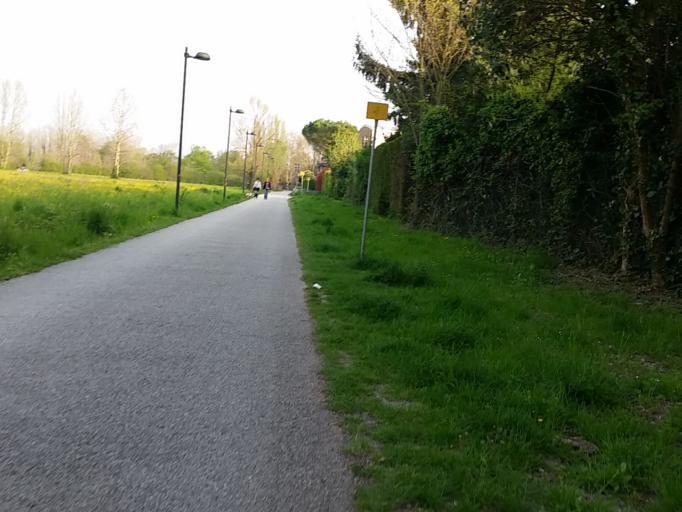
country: IT
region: Veneto
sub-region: Provincia di Padova
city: Padova
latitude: 45.3949
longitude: 11.8953
